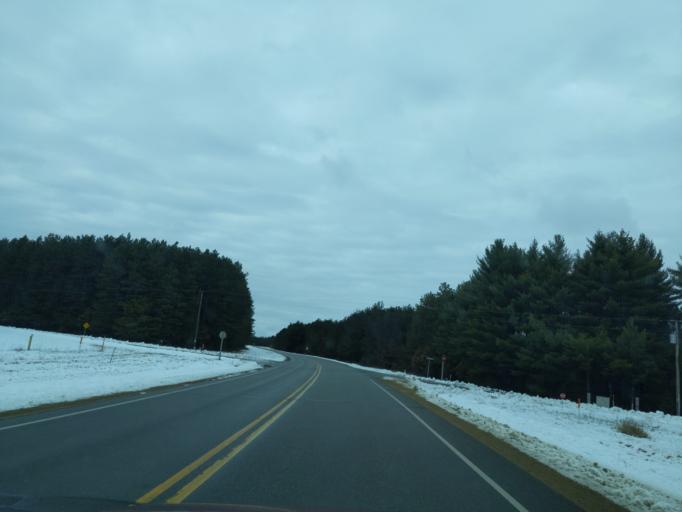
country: US
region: Wisconsin
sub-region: Waushara County
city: Wautoma
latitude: 43.9591
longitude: -89.3188
